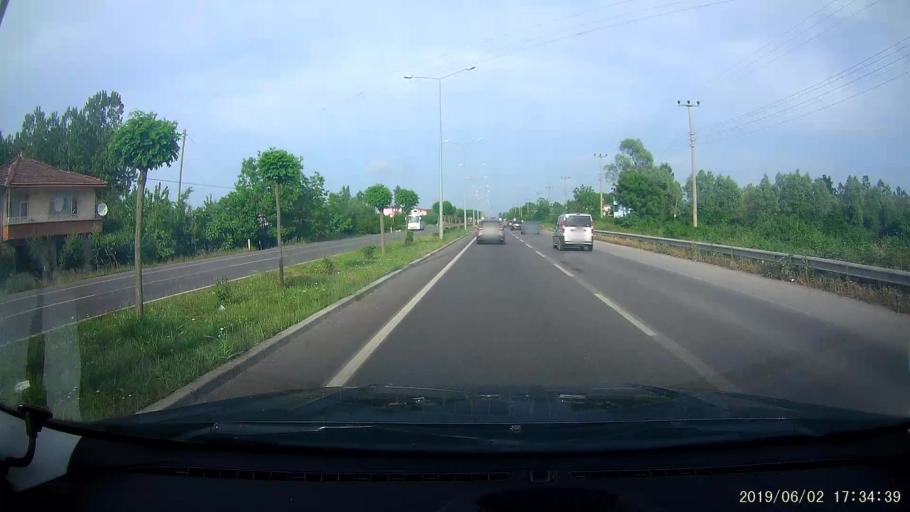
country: TR
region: Samsun
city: Terme
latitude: 41.2200
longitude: 36.8728
